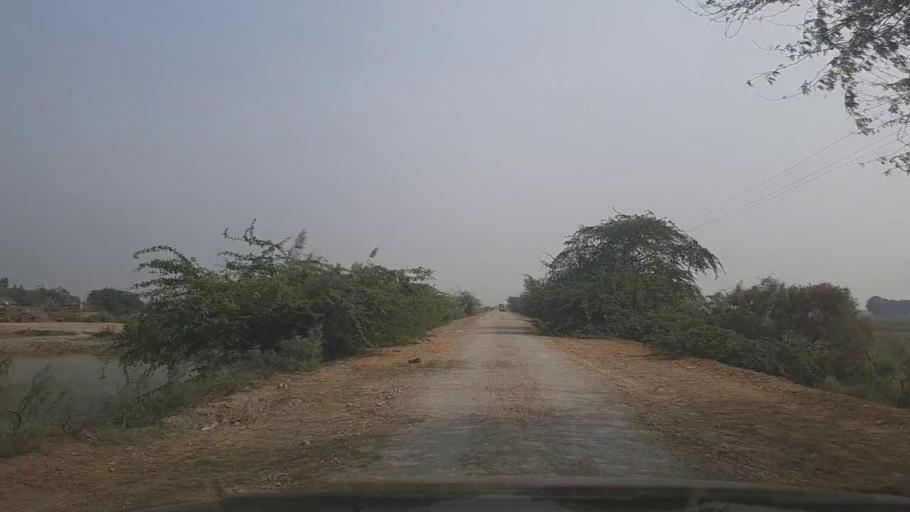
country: PK
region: Sindh
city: Mirpur Sakro
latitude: 24.4793
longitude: 67.6495
